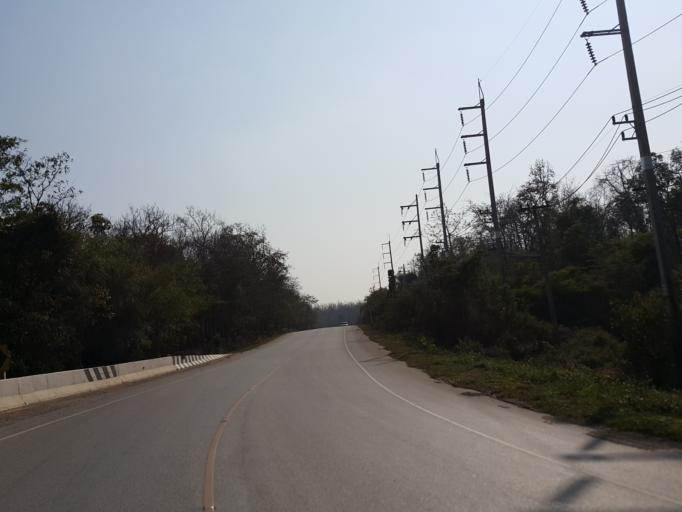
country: TH
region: Lampang
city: Chae Hom
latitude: 18.5480
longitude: 99.5689
